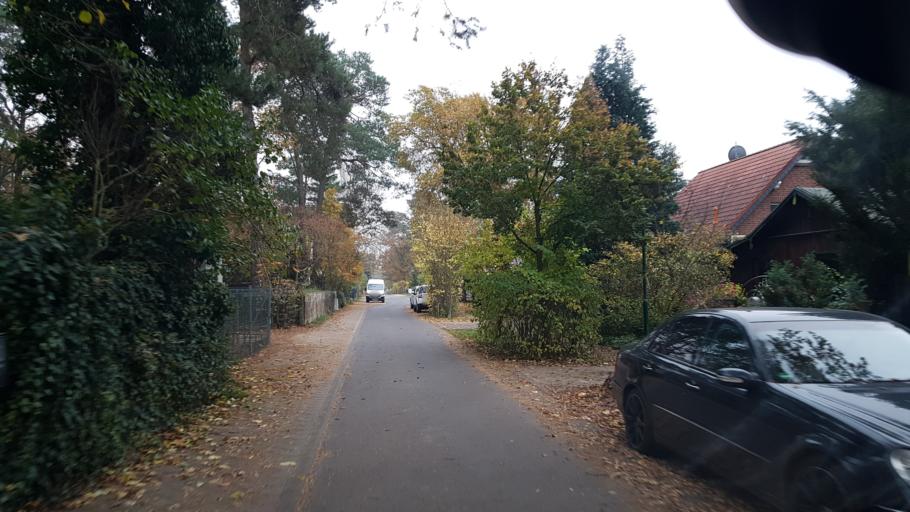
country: DE
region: Berlin
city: Wannsee
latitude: 52.3800
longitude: 13.1611
